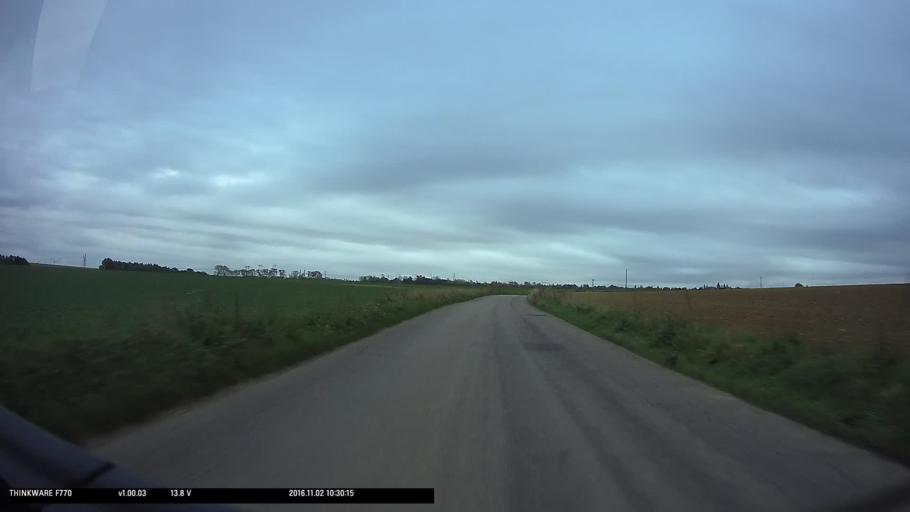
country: FR
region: Ile-de-France
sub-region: Departement du Val-d'Oise
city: Ableiges
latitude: 49.0690
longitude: 2.0050
